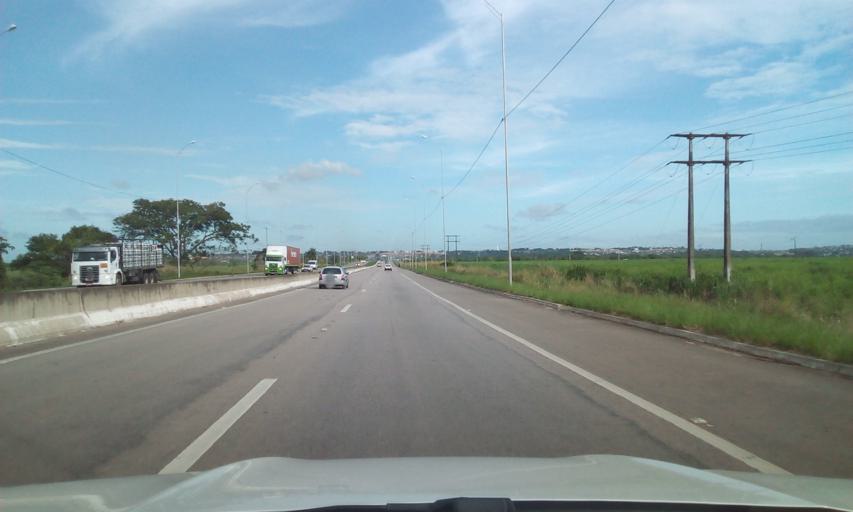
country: BR
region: Paraiba
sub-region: Santa Rita
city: Santa Rita
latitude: -7.0957
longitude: -34.9672
